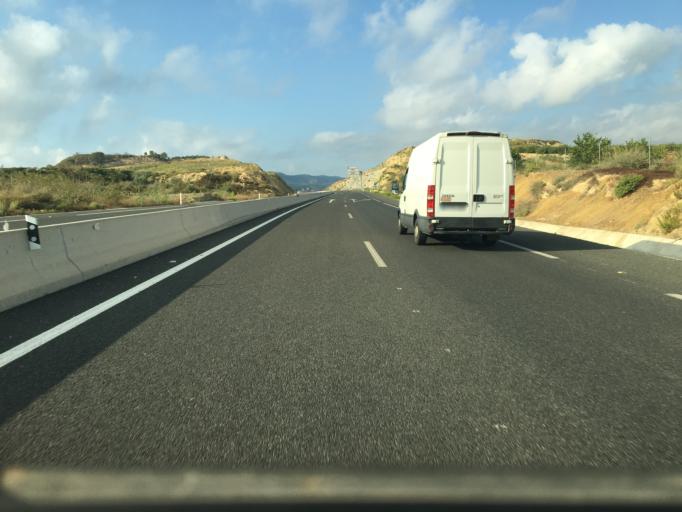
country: ES
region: Murcia
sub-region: Murcia
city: Beniel
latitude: 37.9854
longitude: -0.9740
